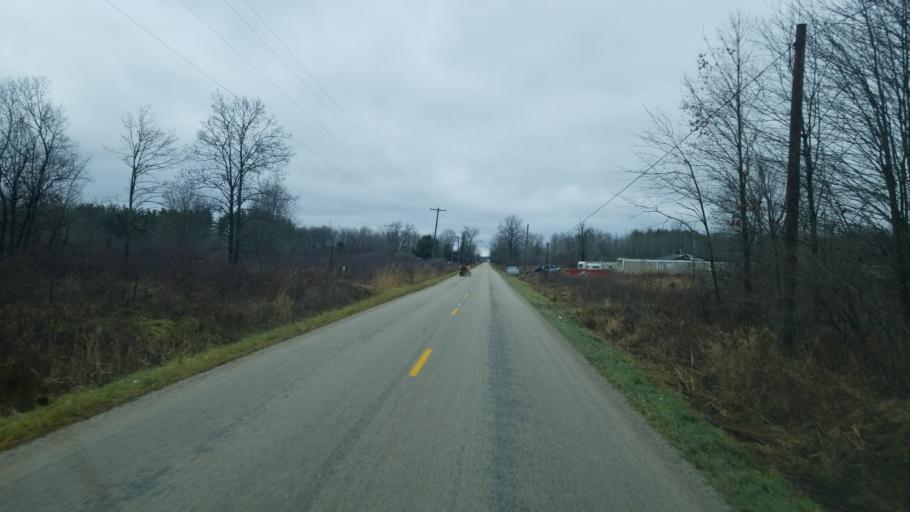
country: US
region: Ohio
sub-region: Ashtabula County
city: Andover
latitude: 41.6636
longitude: -80.6160
